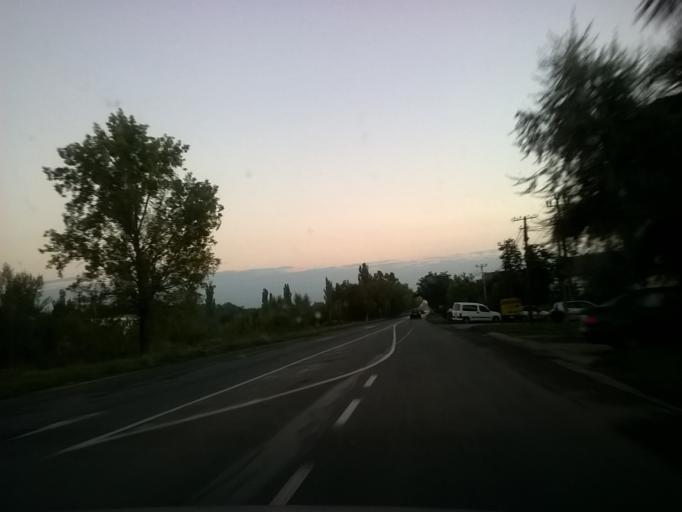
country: RS
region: Autonomna Pokrajina Vojvodina
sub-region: Juznobanatski Okrug
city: Pancevo
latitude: 44.8966
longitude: 20.6312
